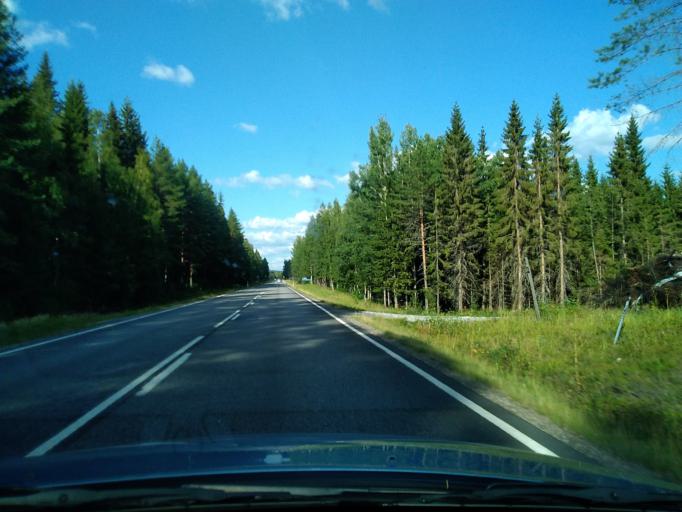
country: FI
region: Pirkanmaa
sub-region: Ylae-Pirkanmaa
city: Maenttae
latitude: 61.9684
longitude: 24.5984
